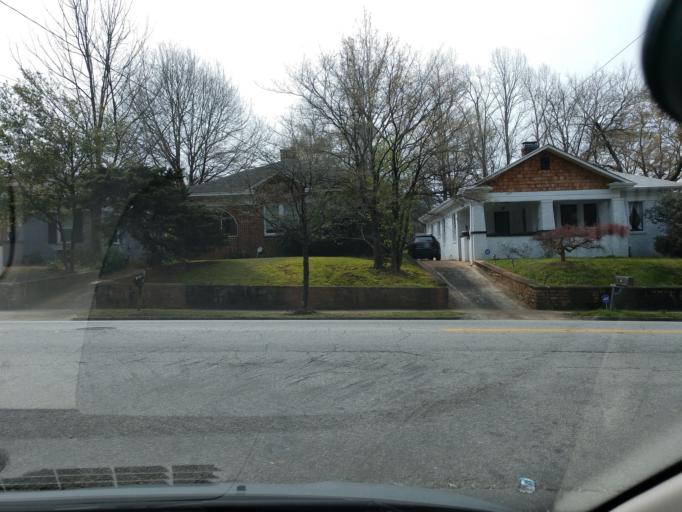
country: US
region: Georgia
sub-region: Fulton County
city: Atlanta
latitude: 33.7269
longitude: -84.3584
